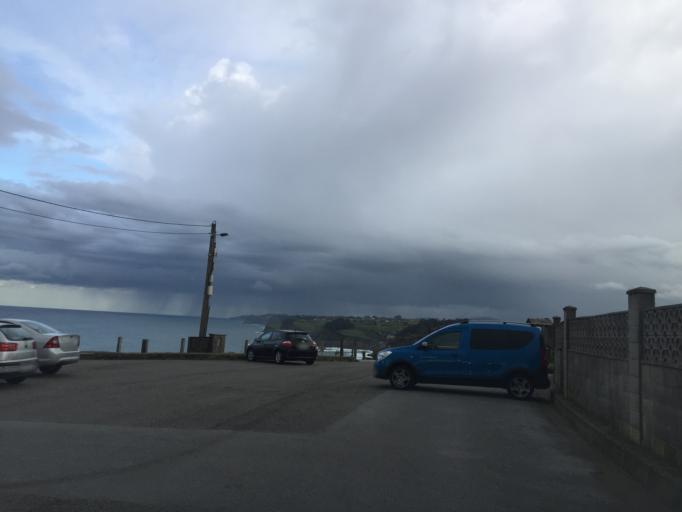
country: ES
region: Asturias
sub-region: Province of Asturias
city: Gijon
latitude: 43.5518
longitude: -5.6147
